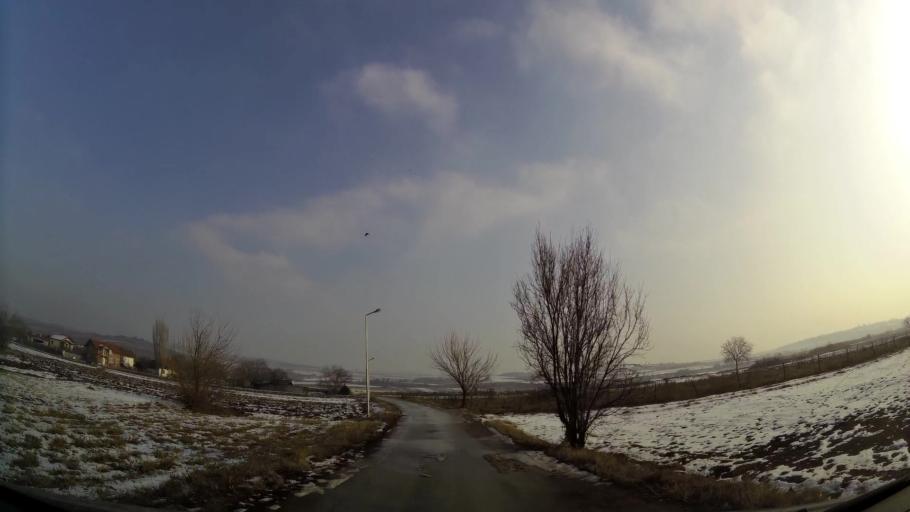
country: MK
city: Miladinovci
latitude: 41.9747
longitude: 21.6413
